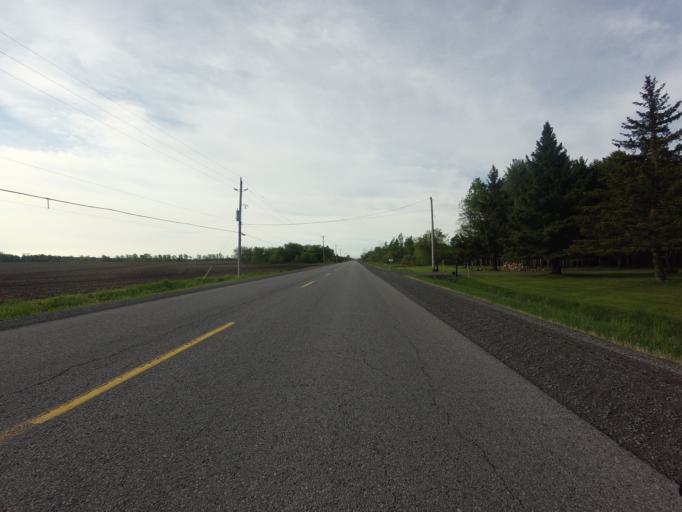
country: CA
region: Ontario
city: Ottawa
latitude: 45.3098
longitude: -75.4589
